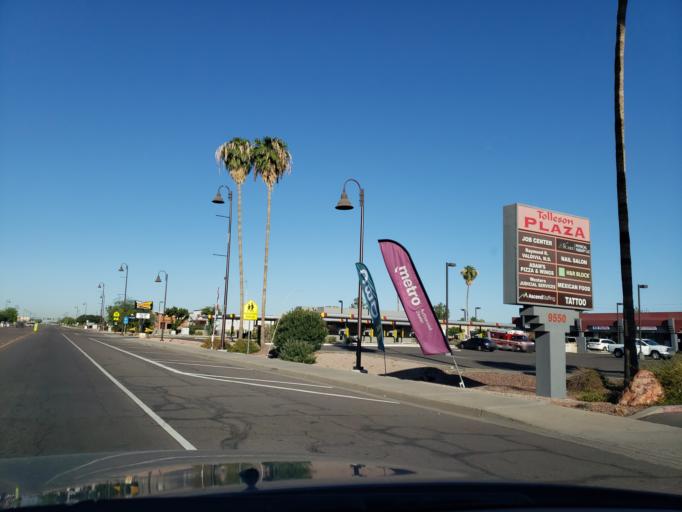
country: US
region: Arizona
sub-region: Maricopa County
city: Tolleson
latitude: 33.4503
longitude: -112.2649
